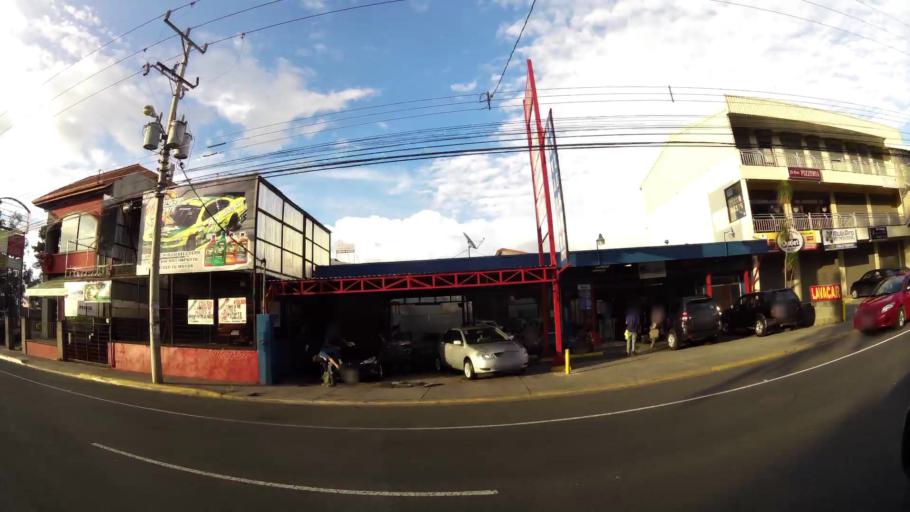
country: CR
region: Heredia
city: San Francisco
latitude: 9.9962
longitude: -84.1314
